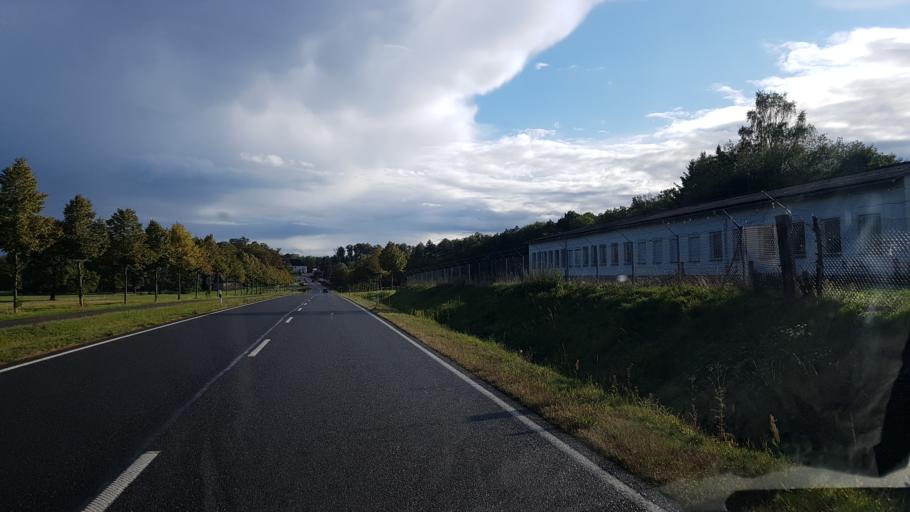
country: DE
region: Saxony
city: Dahlen
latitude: 51.3745
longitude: 12.9936
